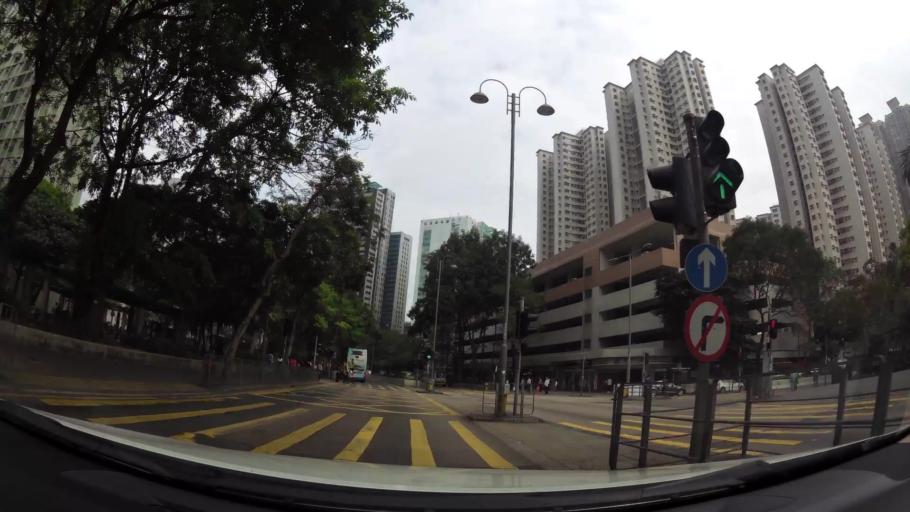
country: HK
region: Wanchai
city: Wan Chai
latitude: 22.2640
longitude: 114.2486
